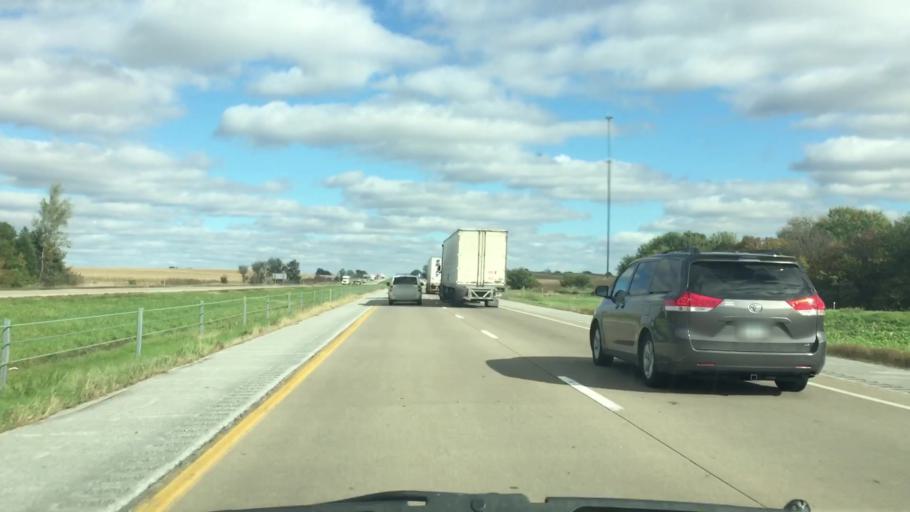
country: US
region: Iowa
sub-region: Muscatine County
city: Wilton
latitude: 41.6448
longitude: -91.1091
